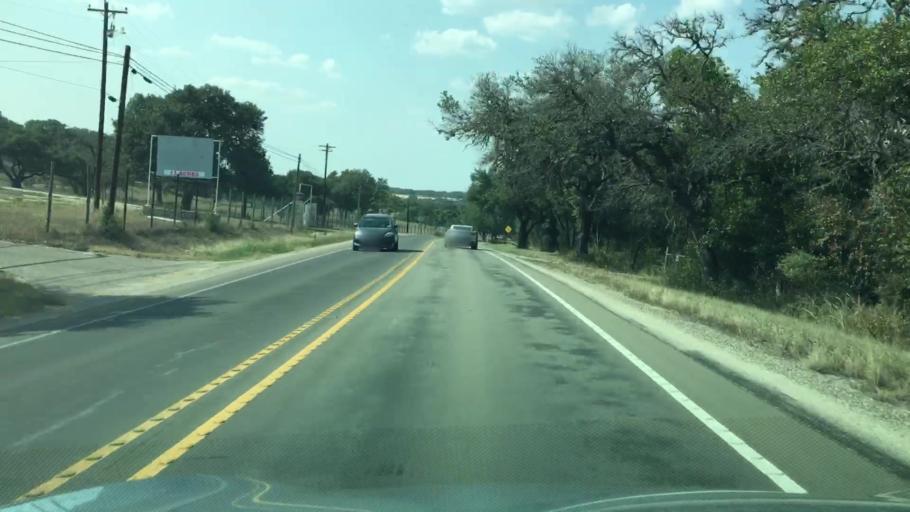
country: US
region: Texas
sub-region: Hays County
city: Dripping Springs
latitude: 30.1554
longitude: -98.0903
